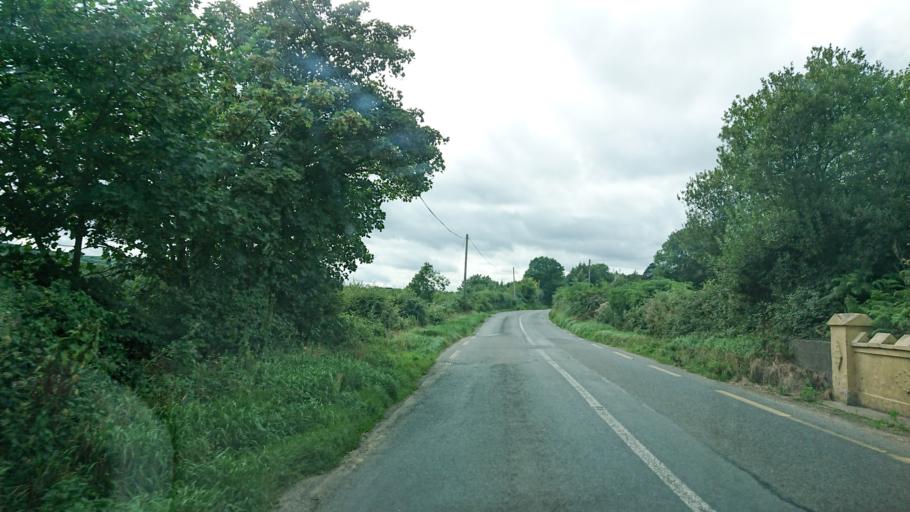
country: IE
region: Munster
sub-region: County Cork
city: Mallow
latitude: 52.1526
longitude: -8.5398
